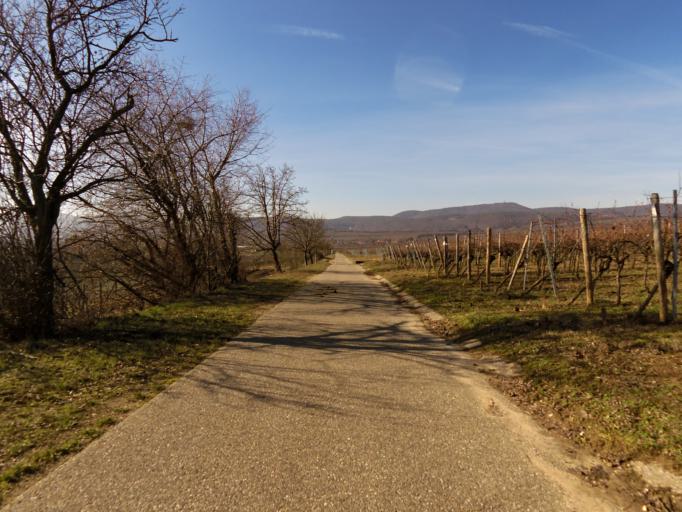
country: DE
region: Rheinland-Pfalz
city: Kallstadt
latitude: 49.4853
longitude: 8.1947
